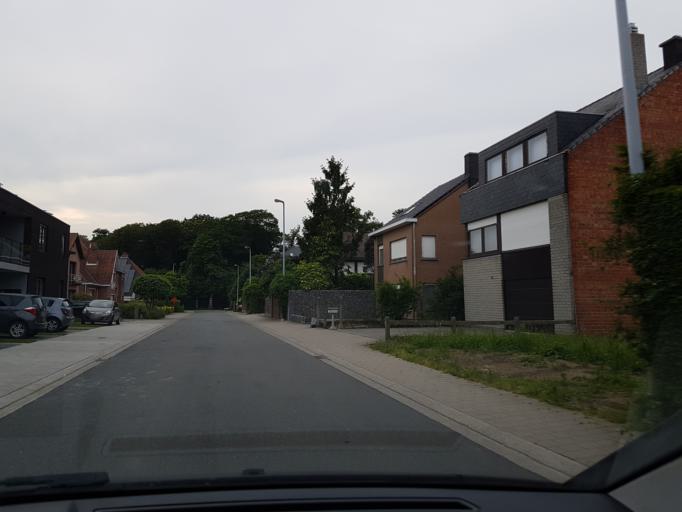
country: BE
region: Flanders
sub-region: Provincie Oost-Vlaanderen
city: Dendermonde
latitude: 50.9799
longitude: 4.0845
